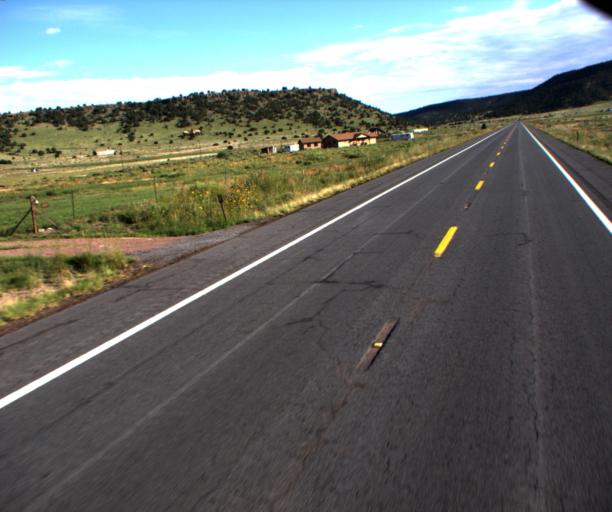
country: US
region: Arizona
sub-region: Apache County
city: Eagar
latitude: 34.0161
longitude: -109.1854
